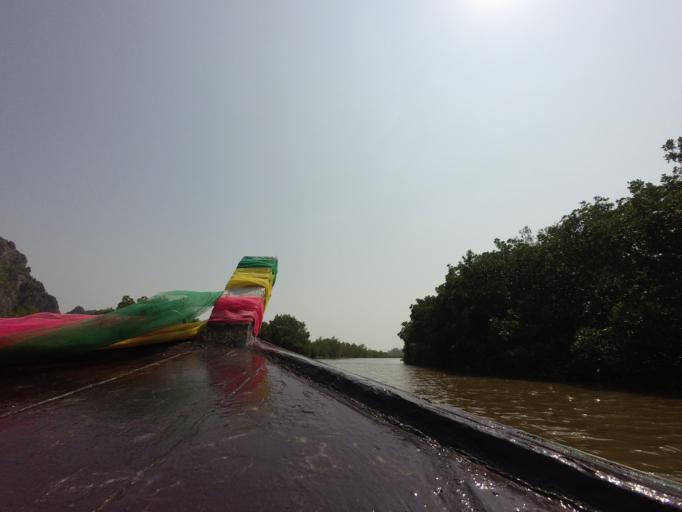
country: TH
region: Prachuap Khiri Khan
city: Kui Buri
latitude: 12.1417
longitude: 99.9562
